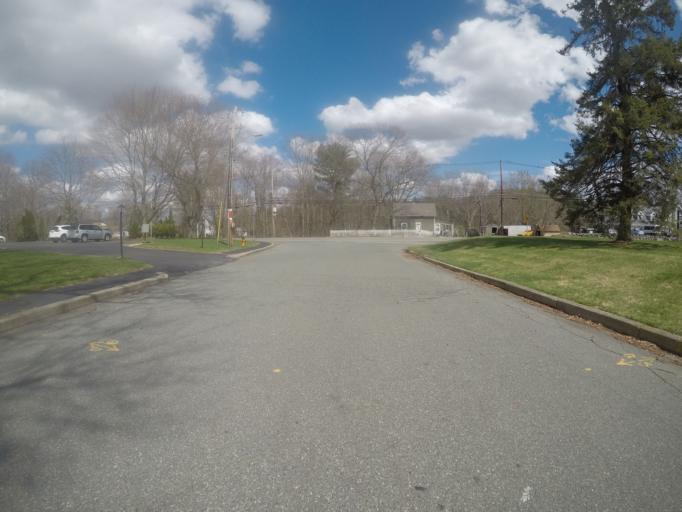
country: US
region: Massachusetts
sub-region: Plymouth County
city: West Bridgewater
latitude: 42.0182
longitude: -71.0671
